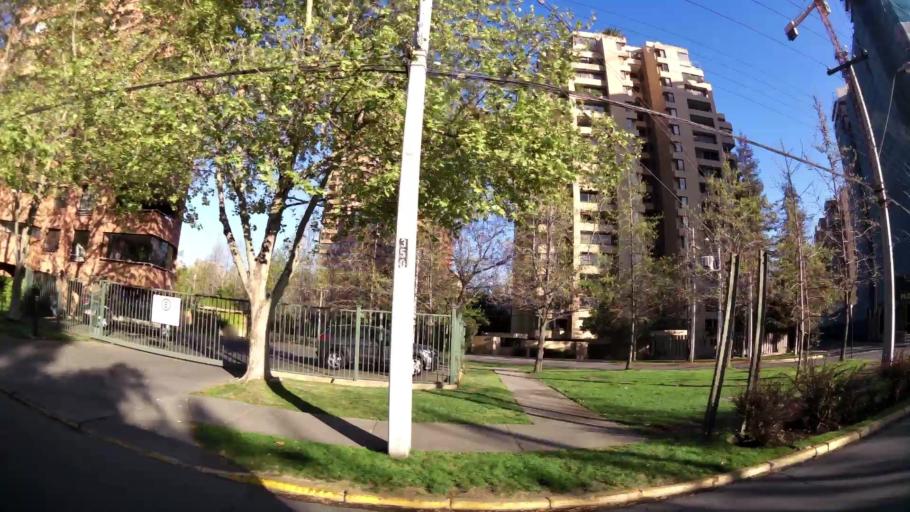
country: CL
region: Santiago Metropolitan
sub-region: Provincia de Santiago
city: Villa Presidente Frei, Nunoa, Santiago, Chile
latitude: -33.3983
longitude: -70.5652
